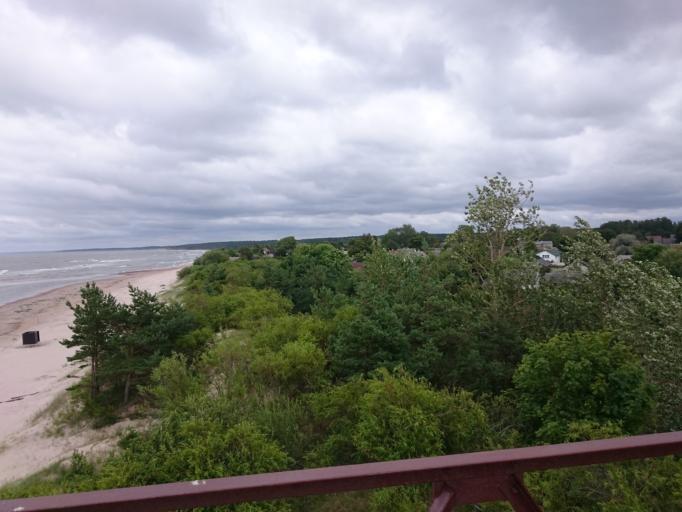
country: LV
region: Pavilostas
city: Pavilosta
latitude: 56.8901
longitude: 21.1728
